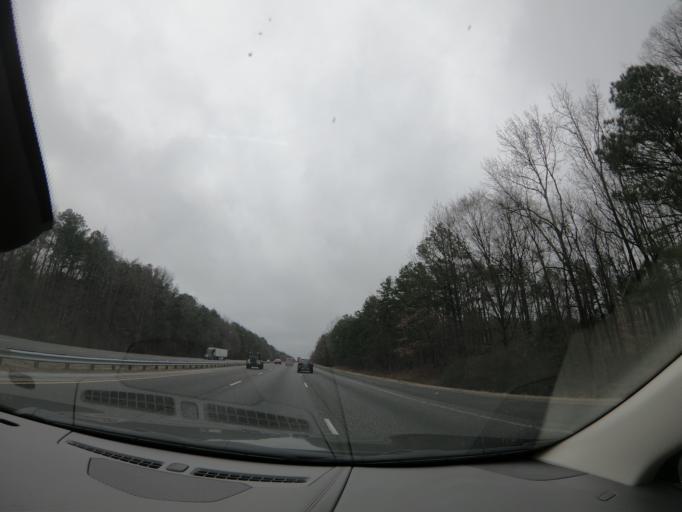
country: US
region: Georgia
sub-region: Whitfield County
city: Dalton
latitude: 34.7088
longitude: -85.0072
